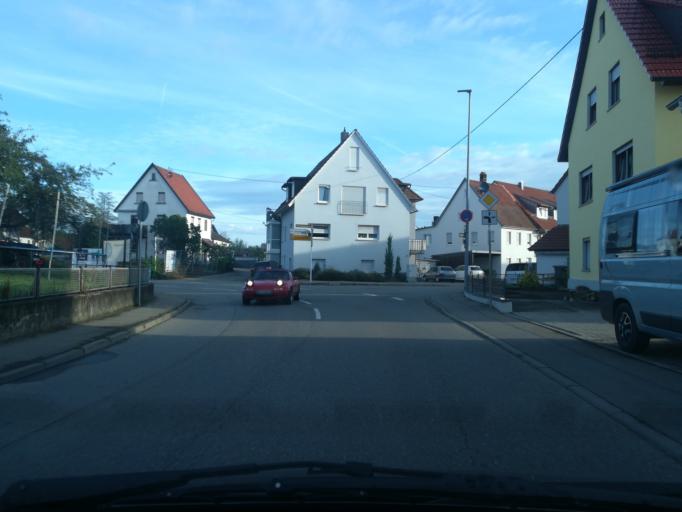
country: DE
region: Baden-Wuerttemberg
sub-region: Tuebingen Region
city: Sickenhausen
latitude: 48.5239
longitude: 9.1753
